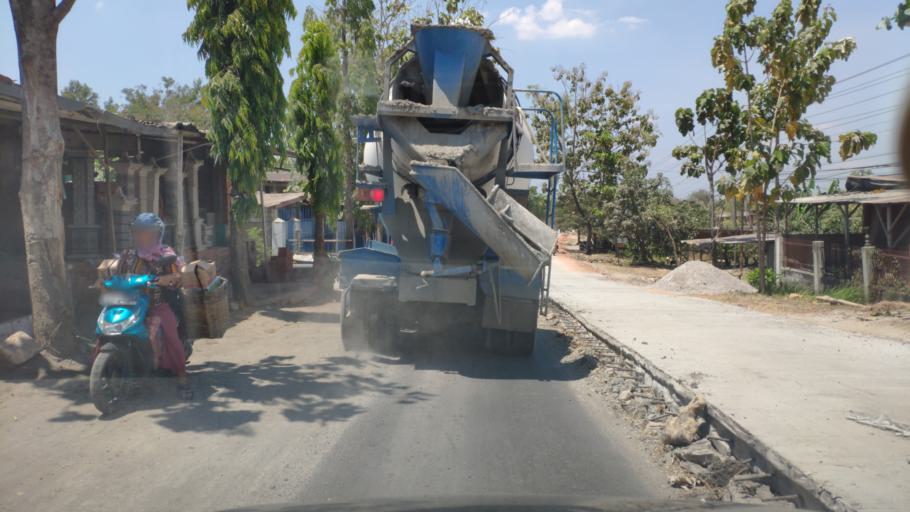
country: ID
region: Central Java
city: Cepu
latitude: -7.1378
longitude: 111.5793
